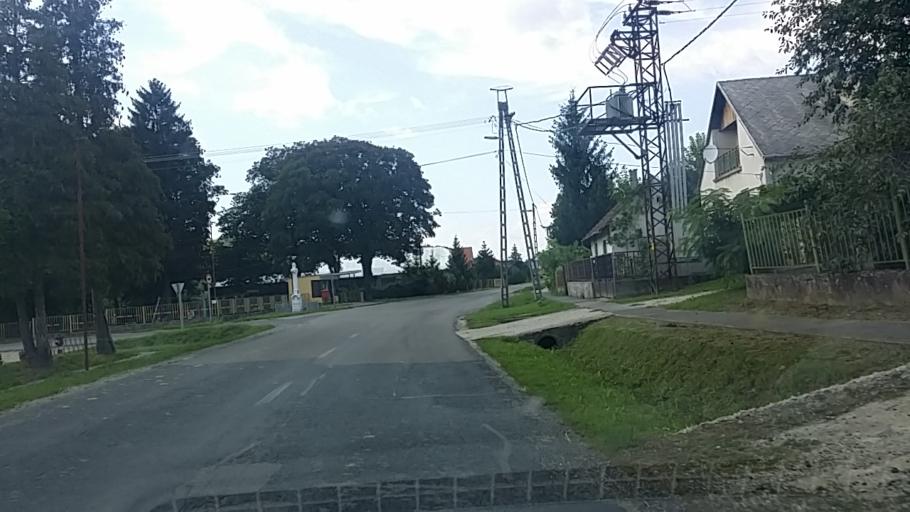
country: HU
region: Zala
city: Becsehely
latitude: 46.4997
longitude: 16.7840
